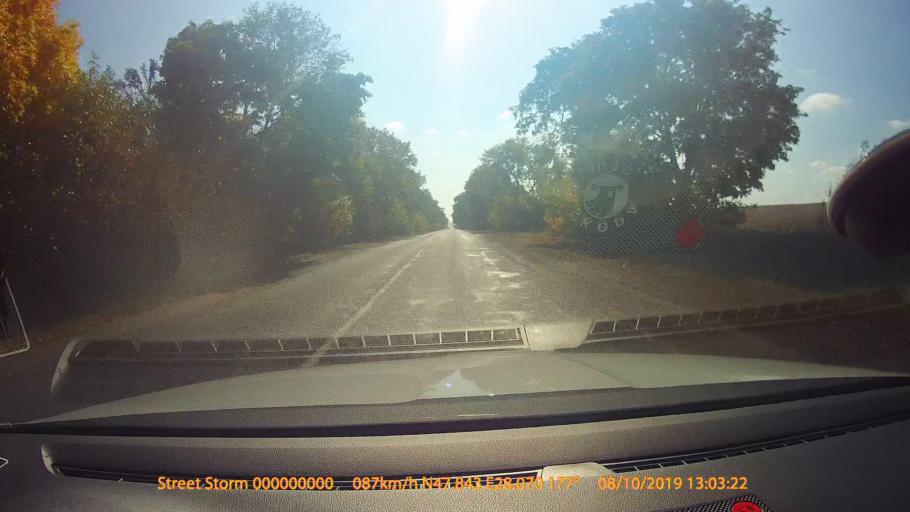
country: MD
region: Singerei
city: Biruinta
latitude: 47.8431
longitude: 28.0696
